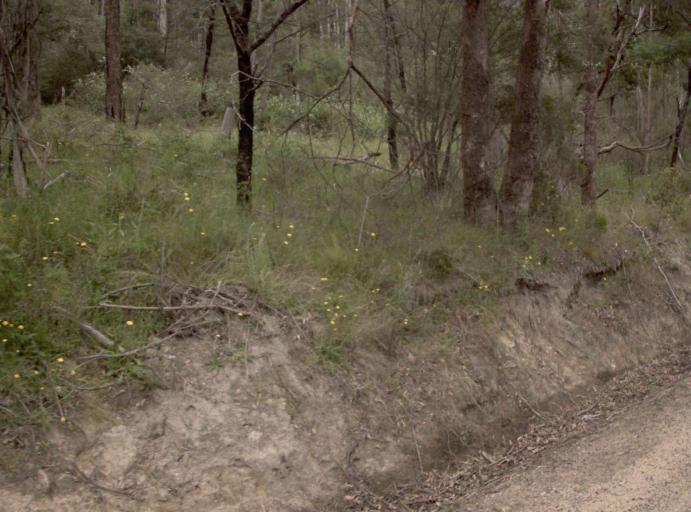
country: AU
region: New South Wales
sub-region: Bombala
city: Bombala
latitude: -37.3996
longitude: 149.1952
